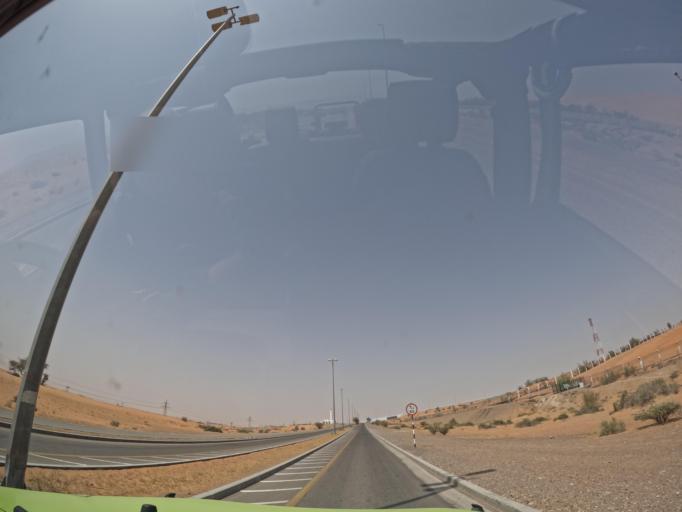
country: OM
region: Al Buraimi
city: Al Buraymi
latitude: 24.7448
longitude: 55.8064
